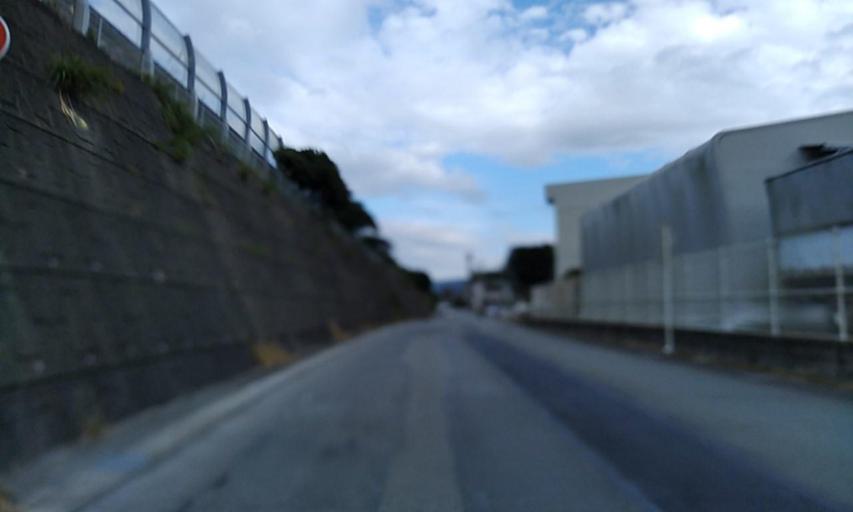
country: JP
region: Shizuoka
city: Gotemba
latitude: 35.2883
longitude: 138.9338
